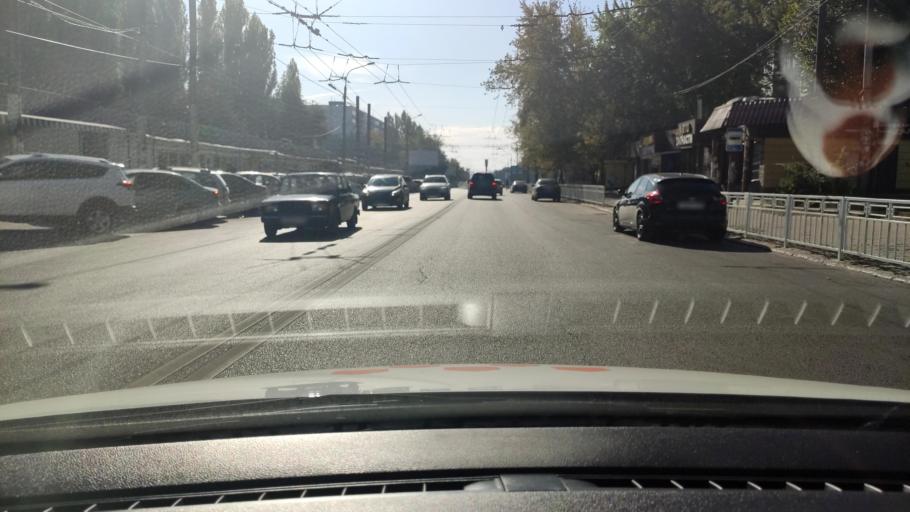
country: RU
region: Voronezj
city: Podgornoye
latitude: 51.7050
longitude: 39.1480
